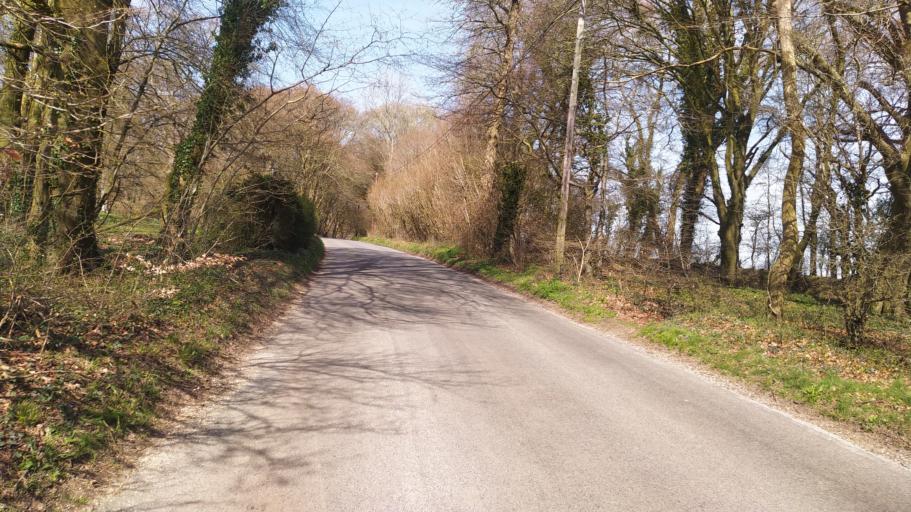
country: GB
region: England
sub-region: Hampshire
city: Four Marks
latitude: 51.0620
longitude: -1.1066
